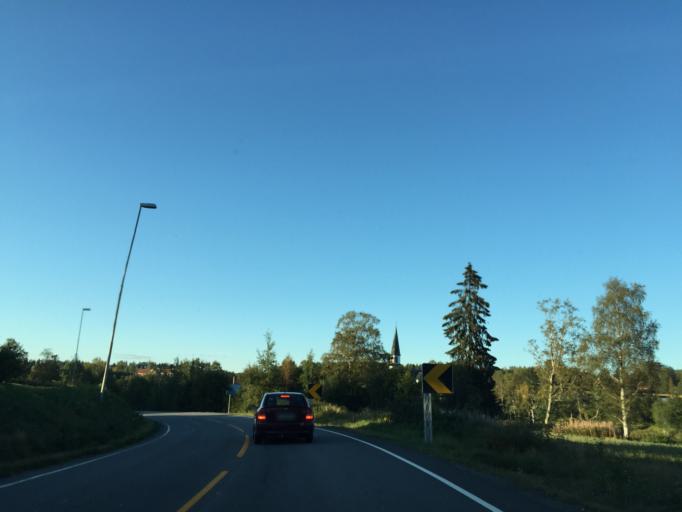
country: NO
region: Hedmark
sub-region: Nord-Odal
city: Sand
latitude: 60.3867
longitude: 11.5423
